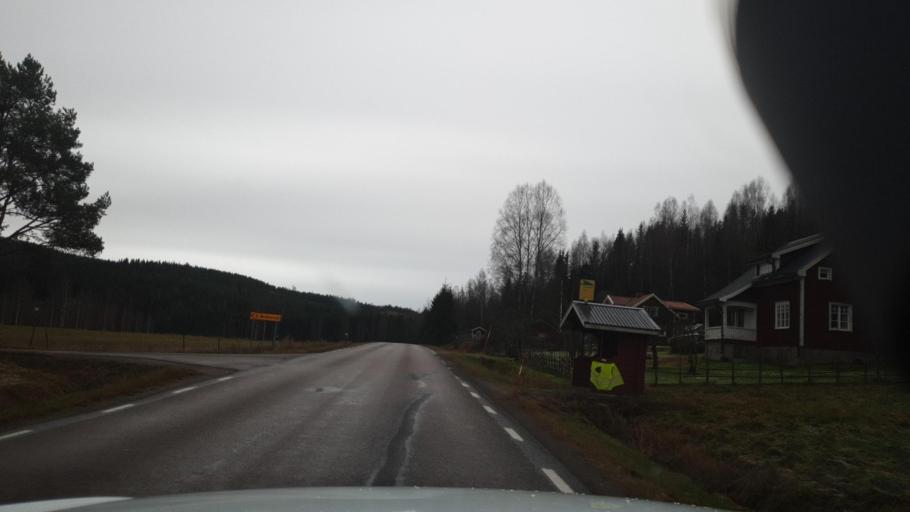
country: SE
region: Vaermland
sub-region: Arvika Kommun
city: Arvika
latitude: 59.7240
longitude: 12.7982
